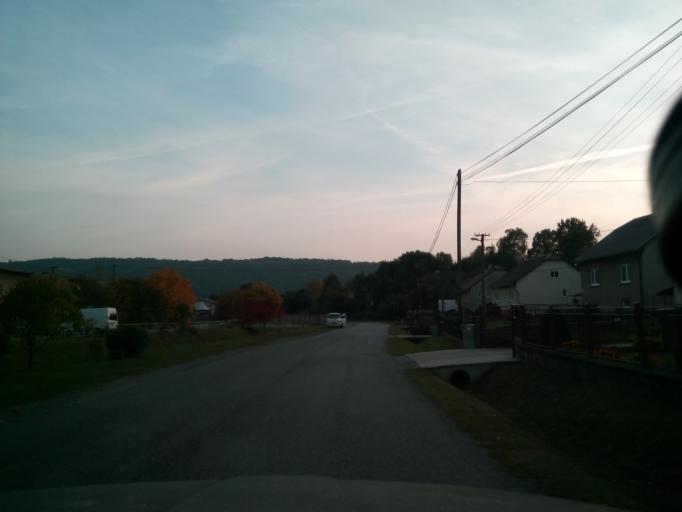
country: SK
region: Presovsky
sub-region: Okres Bardejov
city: Bardejov
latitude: 49.3088
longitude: 21.3172
